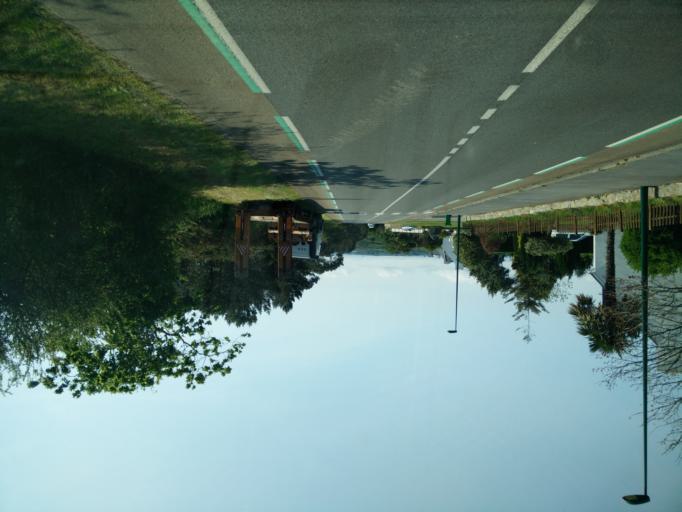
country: FR
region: Brittany
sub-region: Departement du Finistere
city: Crozon
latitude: 48.2435
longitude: -4.4771
